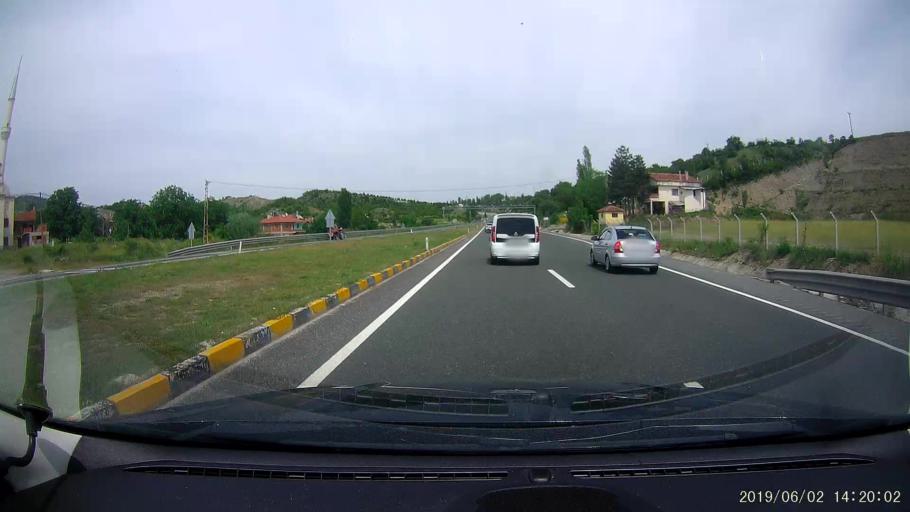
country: TR
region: Kastamonu
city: Tosya
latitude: 40.9679
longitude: 33.9840
